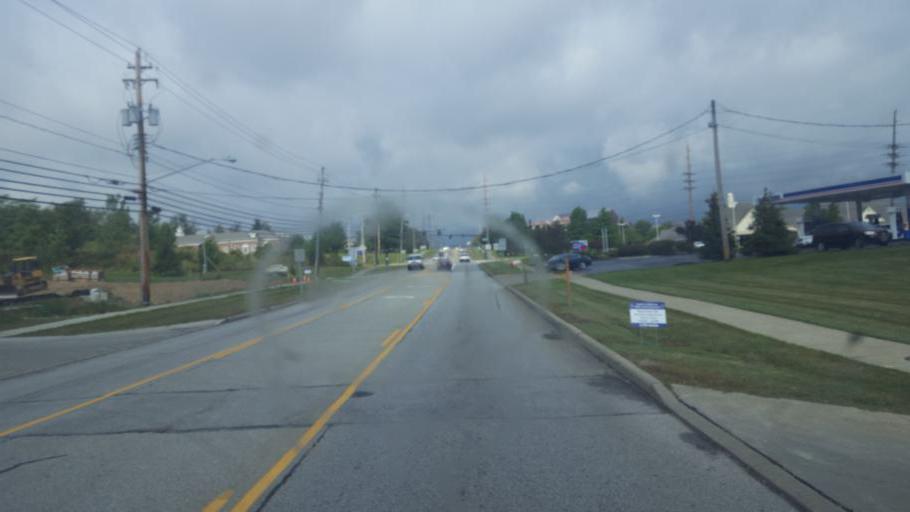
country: US
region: Ohio
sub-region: Geauga County
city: Chardon
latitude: 41.5862
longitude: -81.2176
